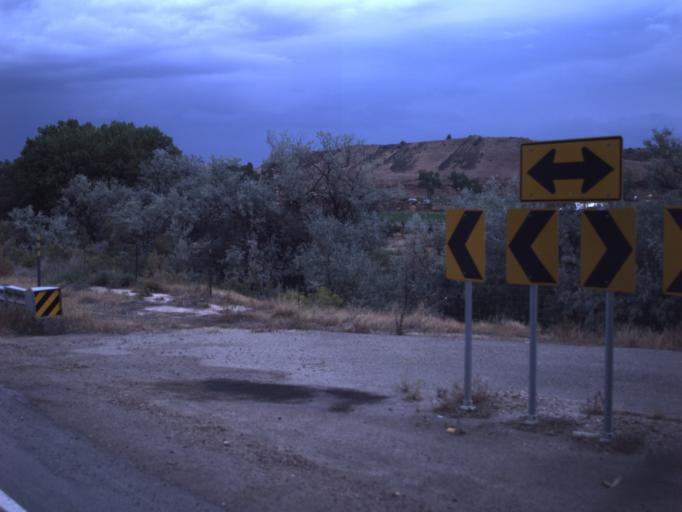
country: US
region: Utah
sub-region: Duchesne County
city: Roosevelt
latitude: 40.3125
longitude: -110.0113
